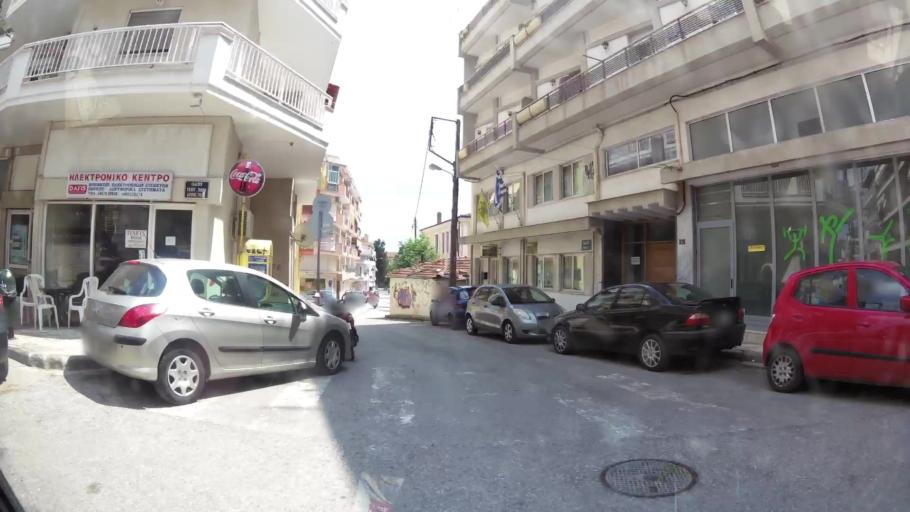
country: GR
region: West Macedonia
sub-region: Nomos Kozanis
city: Kozani
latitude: 40.2973
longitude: 21.7886
